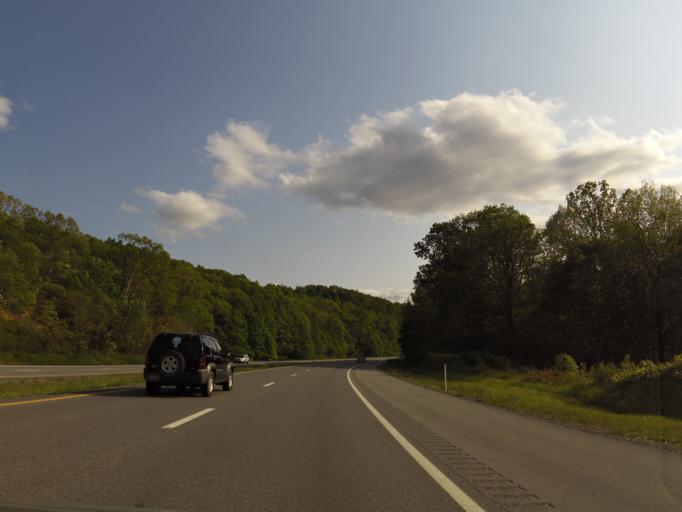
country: US
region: West Virginia
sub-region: Mercer County
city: Princeton
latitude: 37.3062
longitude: -81.1389
